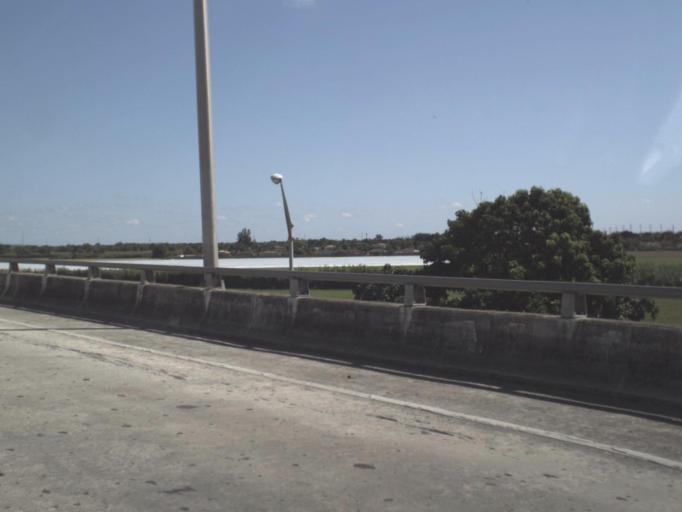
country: US
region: Florida
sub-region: Miami-Dade County
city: Naranja
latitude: 25.5102
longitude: -80.4128
